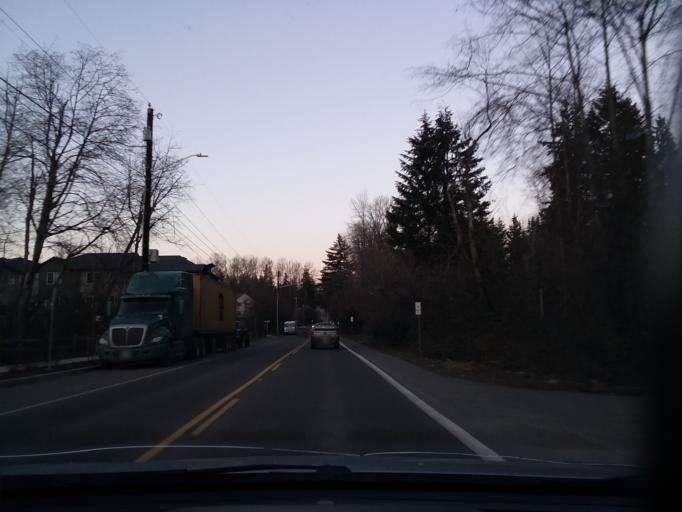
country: US
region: Washington
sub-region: Snohomish County
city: Martha Lake
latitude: 47.8792
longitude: -122.2599
